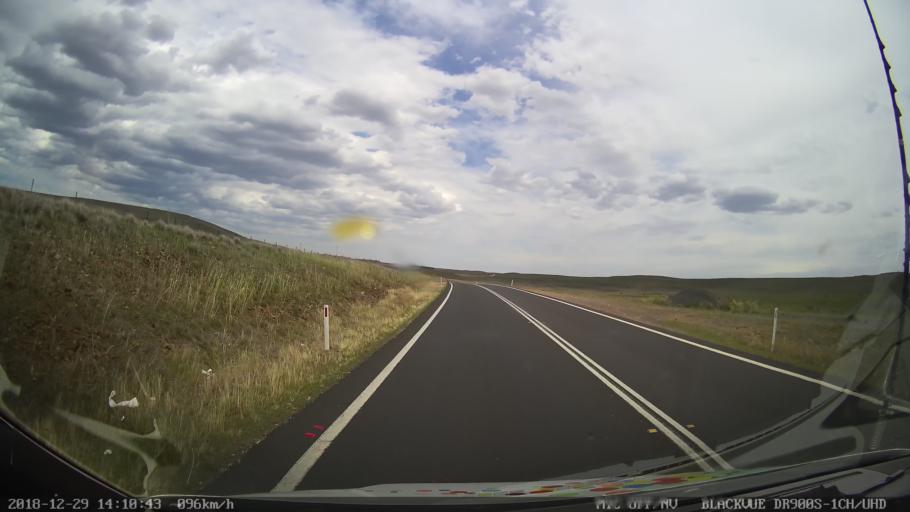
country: AU
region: New South Wales
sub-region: Cooma-Monaro
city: Cooma
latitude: -36.3957
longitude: 149.2164
